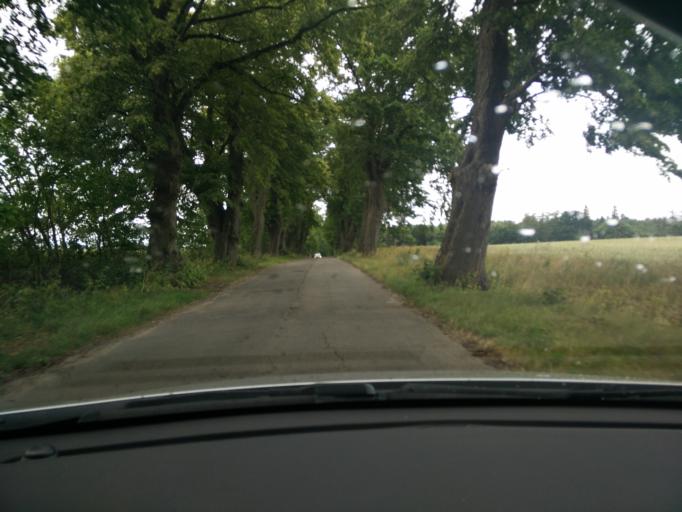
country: PL
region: Pomeranian Voivodeship
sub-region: Powiat pucki
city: Mrzezino
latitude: 54.6736
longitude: 18.4582
